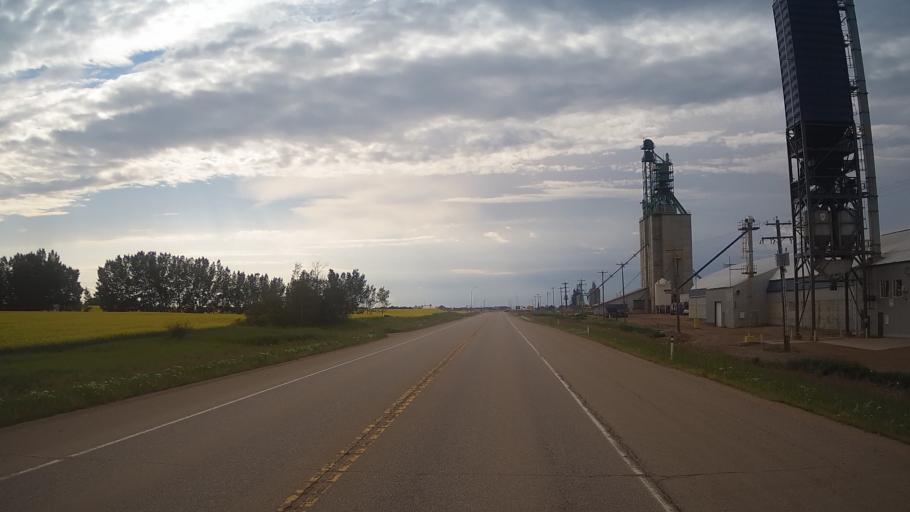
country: CA
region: Alberta
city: Viking
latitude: 53.0903
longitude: -111.7744
